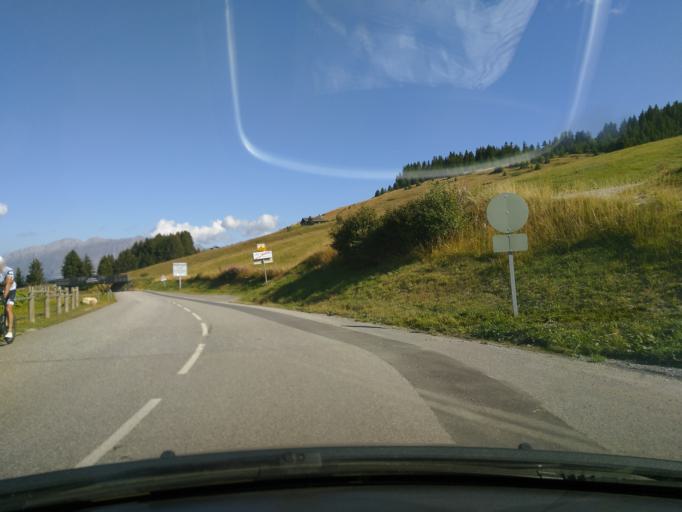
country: FR
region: Rhone-Alpes
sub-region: Departement de la Savoie
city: Beaufort
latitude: 45.7636
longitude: 6.5339
